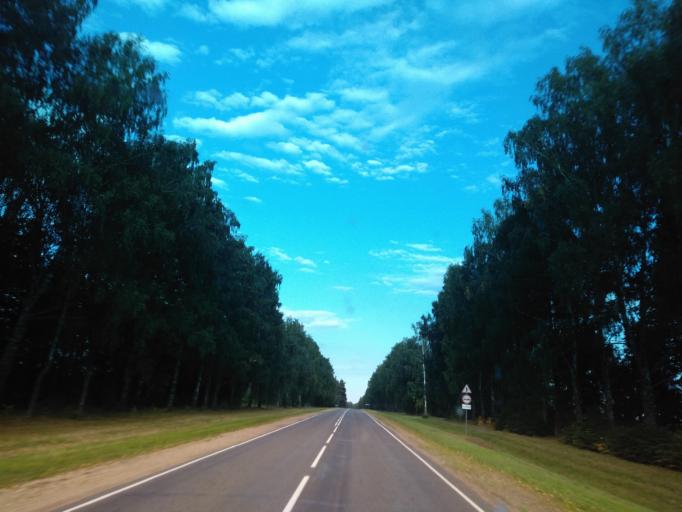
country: BY
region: Minsk
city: Uzda
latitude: 53.4259
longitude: 27.3671
